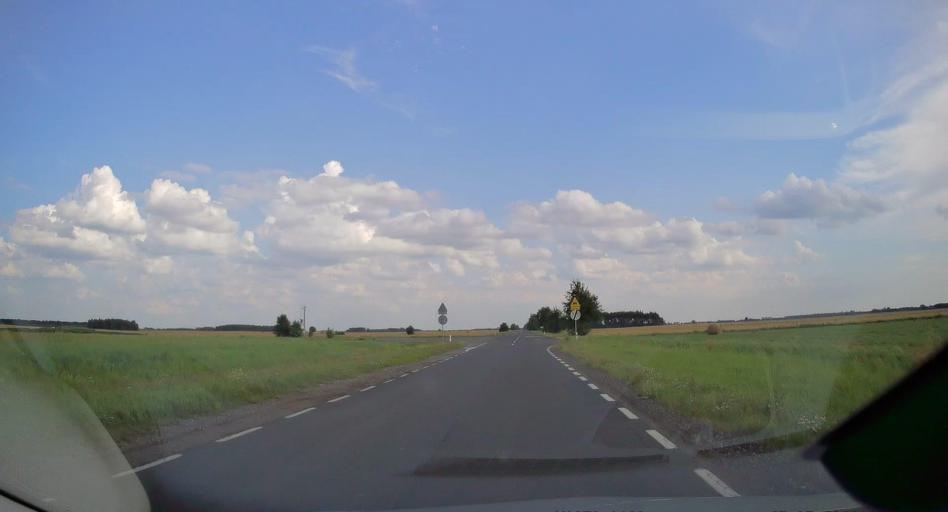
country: PL
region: Lodz Voivodeship
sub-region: Powiat tomaszowski
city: Rzeczyca
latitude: 51.6655
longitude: 20.2655
